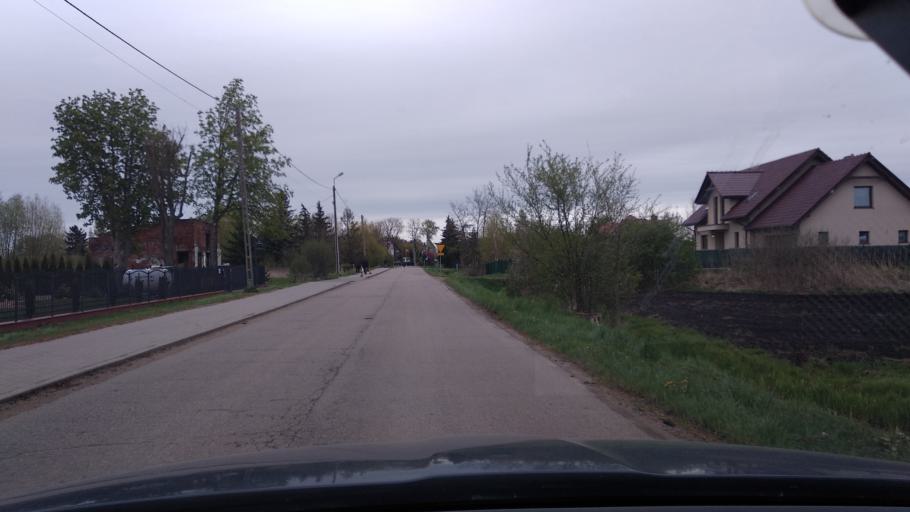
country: PL
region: Pomeranian Voivodeship
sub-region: Powiat gdanski
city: Pruszcz Gdanski
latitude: 54.2746
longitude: 18.6814
